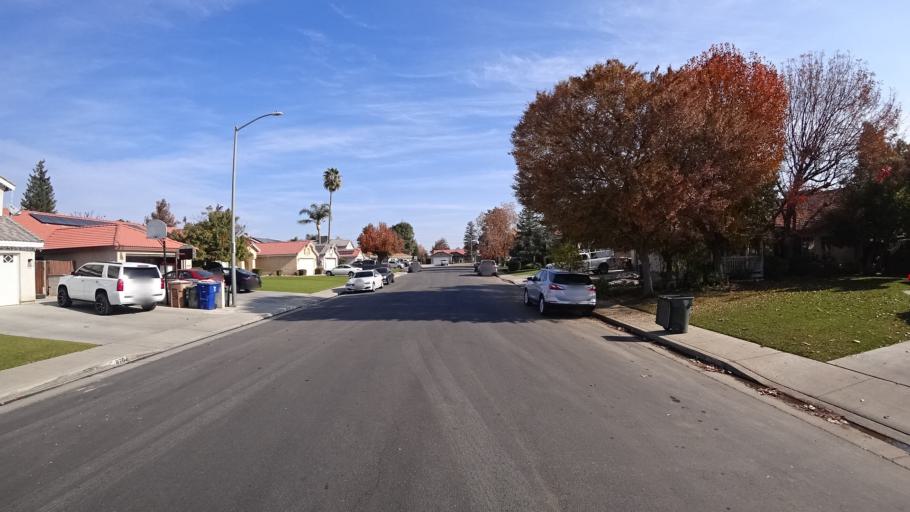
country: US
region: California
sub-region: Kern County
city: Greenacres
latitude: 35.3655
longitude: -119.0993
